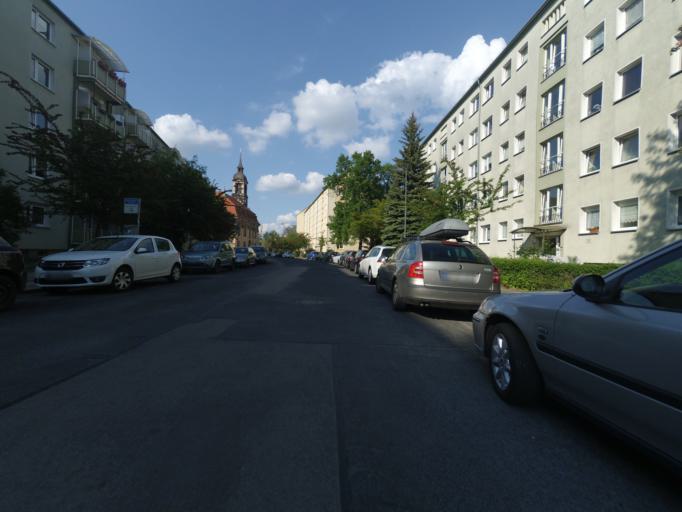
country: DE
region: Saxony
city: Dresden
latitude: 51.0474
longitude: 13.7267
